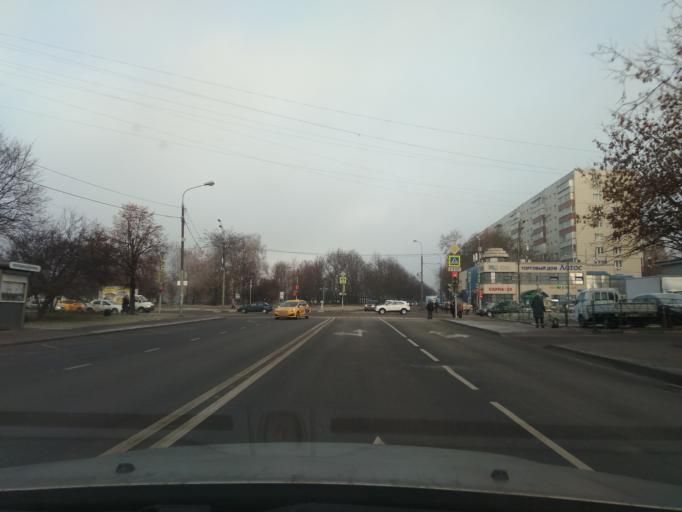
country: RU
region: Moscow
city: Zapadnoye Degunino
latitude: 55.8756
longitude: 37.5339
